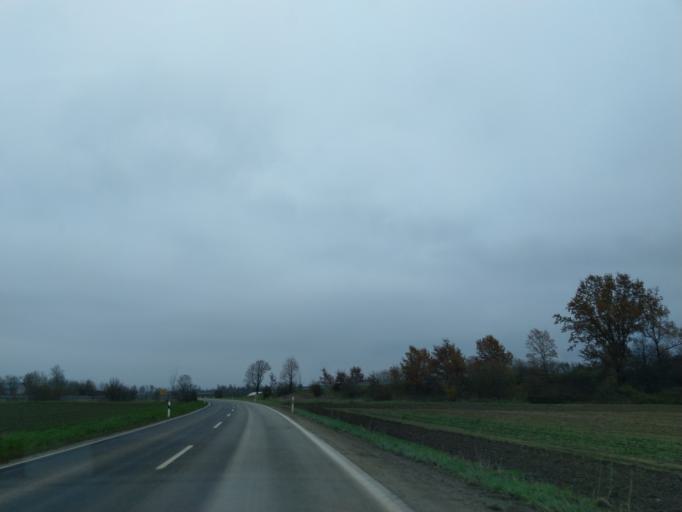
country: DE
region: Bavaria
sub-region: Lower Bavaria
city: Otzing
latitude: 48.7859
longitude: 12.8236
